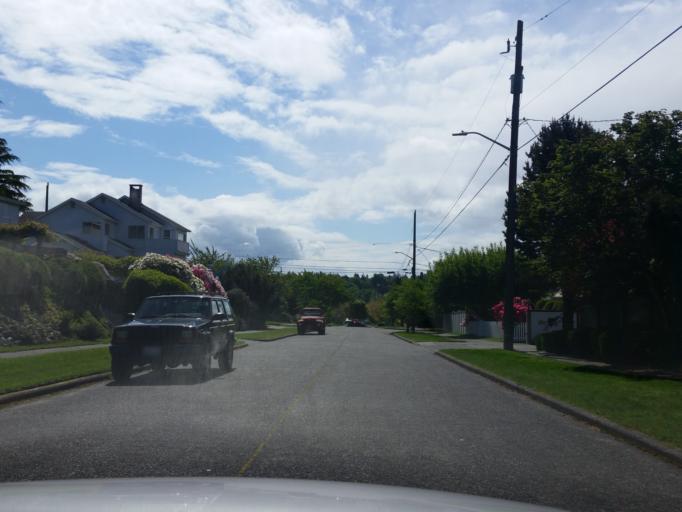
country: US
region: Washington
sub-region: King County
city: Seattle
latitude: 47.6721
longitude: -122.4012
